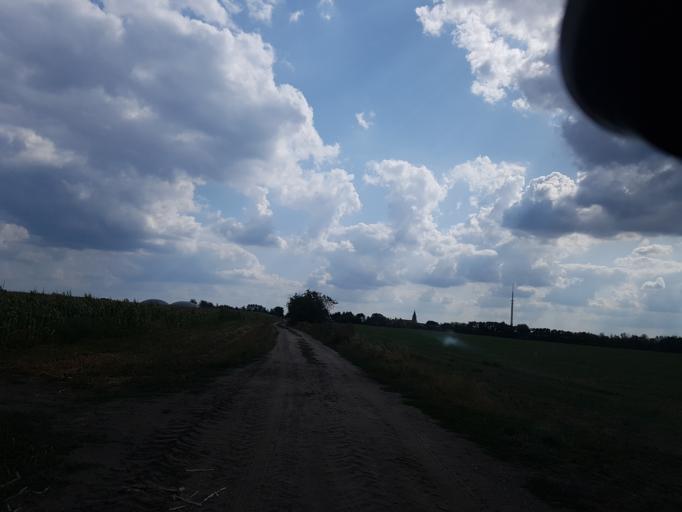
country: DE
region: Brandenburg
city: Calau
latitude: 51.7581
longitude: 13.9513
